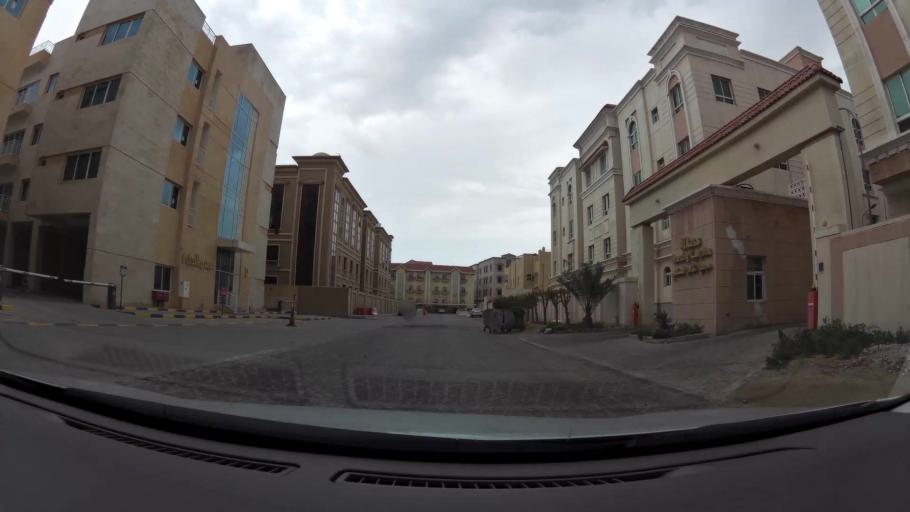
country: QA
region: Baladiyat ad Dawhah
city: Doha
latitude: 25.2776
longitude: 51.4964
